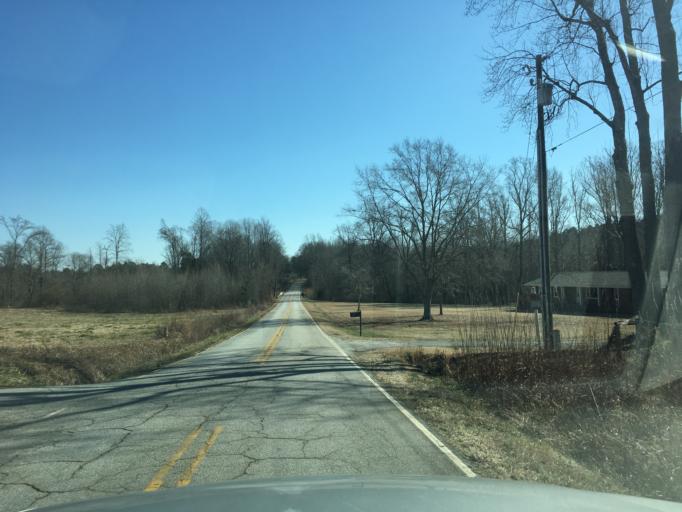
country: US
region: South Carolina
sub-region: Pickens County
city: Pickens
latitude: 34.8425
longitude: -82.7989
